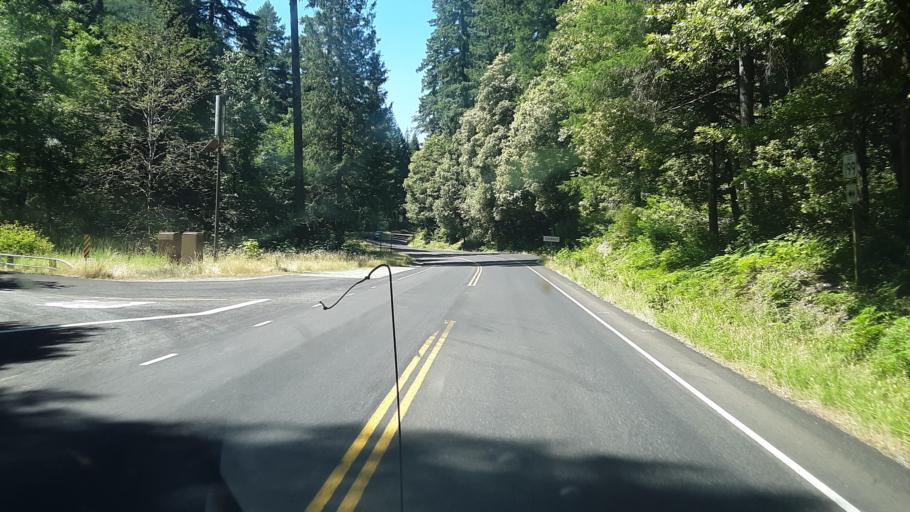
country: US
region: Oregon
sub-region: Josephine County
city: Cave Junction
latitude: 41.9255
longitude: -123.7612
